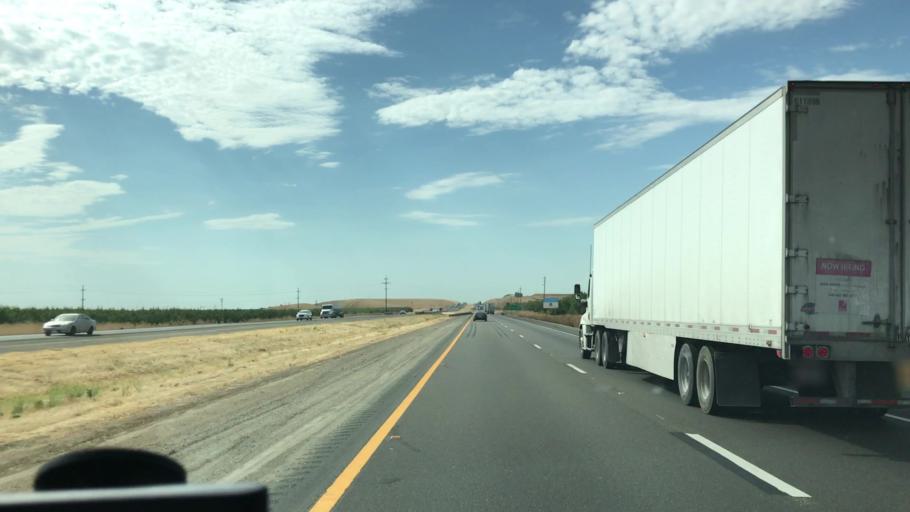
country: US
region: California
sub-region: Stanislaus County
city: Patterson
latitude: 37.4065
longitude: -121.1447
